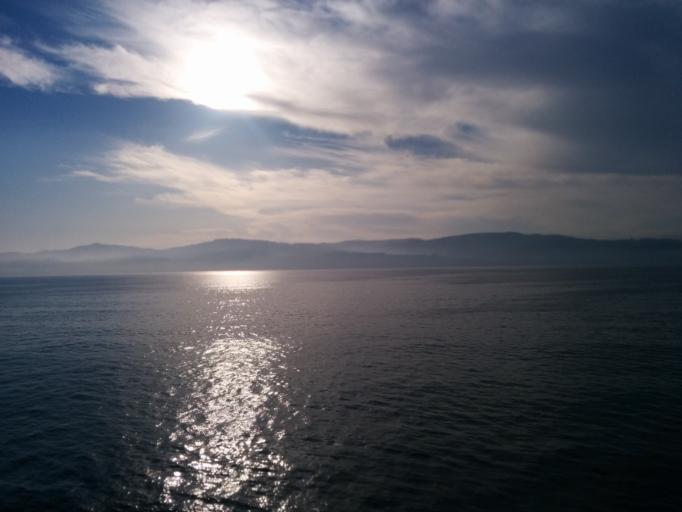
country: MA
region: Tanger-Tetouan
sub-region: Tanger-Assilah
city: Tangier
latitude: 35.8025
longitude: -5.7853
